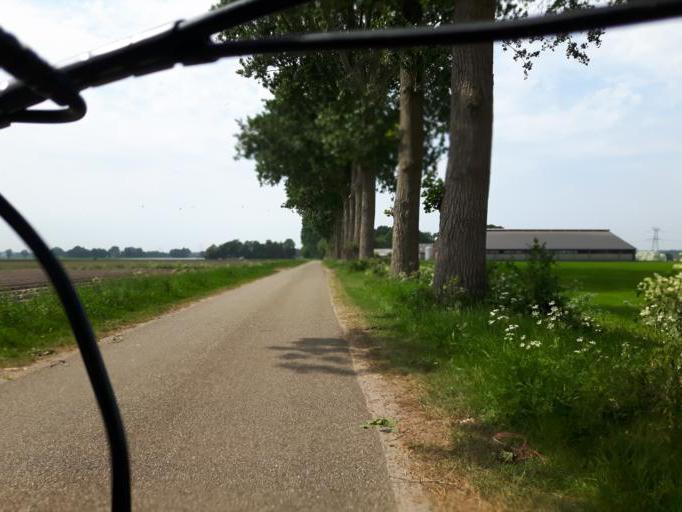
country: NL
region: North Brabant
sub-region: Gemeente Steenbergen
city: Welberg
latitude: 51.5358
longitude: 4.3262
